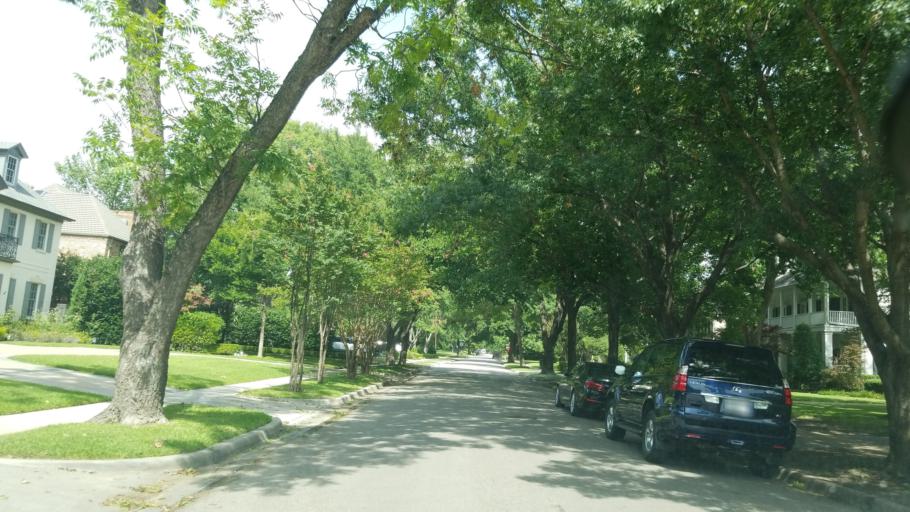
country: US
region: Texas
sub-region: Dallas County
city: University Park
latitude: 32.8560
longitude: -96.7982
